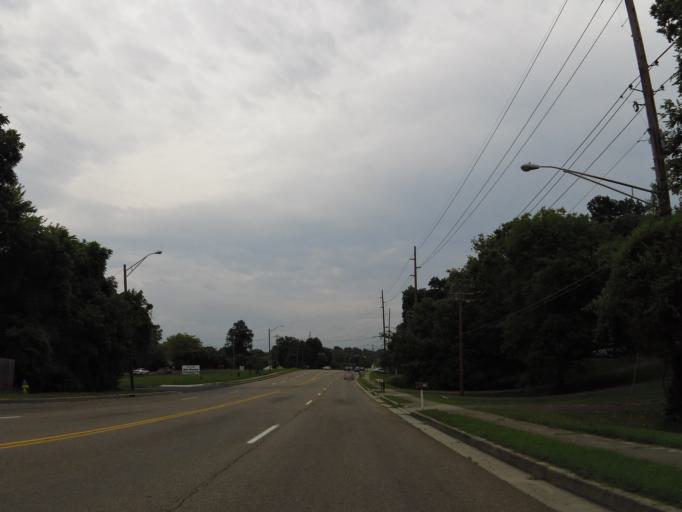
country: US
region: Tennessee
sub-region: Knox County
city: Knoxville
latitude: 35.9422
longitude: -83.9009
